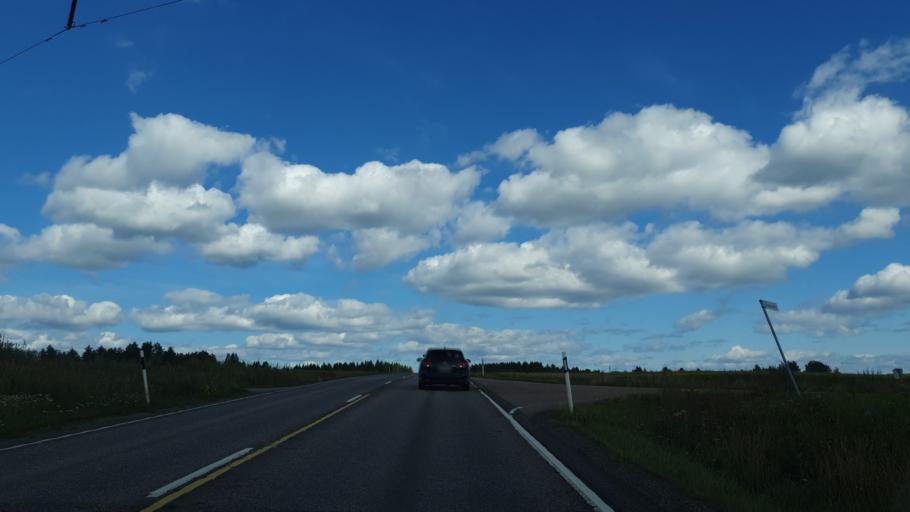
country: FI
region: Central Finland
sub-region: Jaemsae
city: Jaemsae
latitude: 61.8422
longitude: 25.1345
